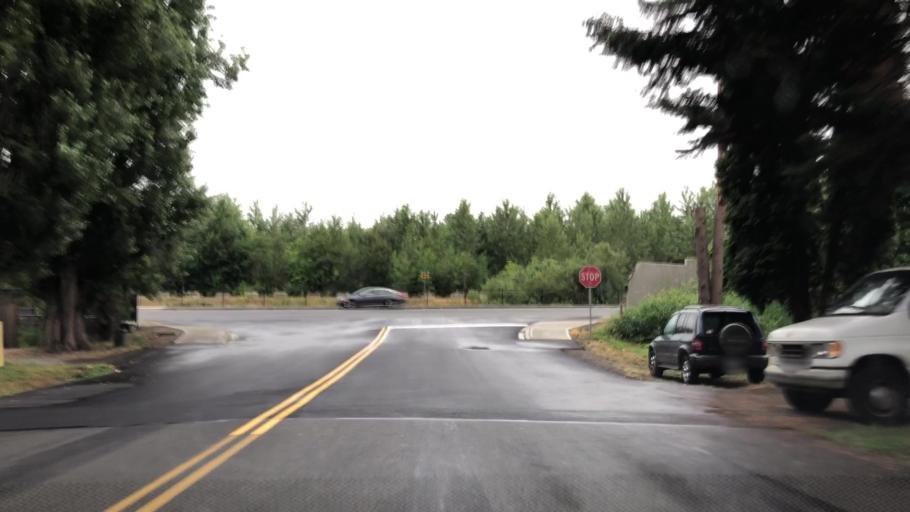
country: US
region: Washington
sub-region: Snohomish County
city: North Creek
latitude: 47.8099
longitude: -122.2136
